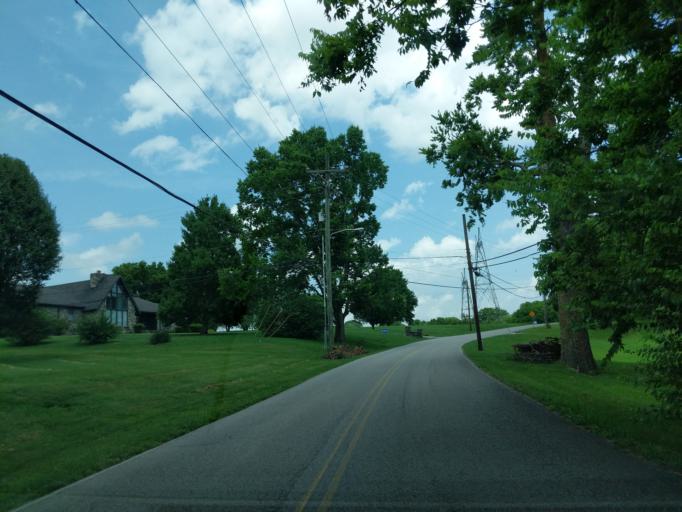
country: US
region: Tennessee
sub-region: Davidson County
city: Goodlettsville
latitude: 36.3039
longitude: -86.7275
